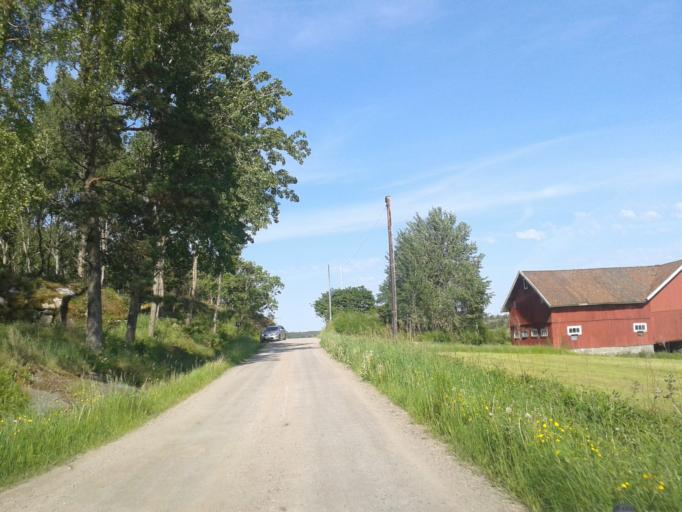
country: SE
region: Vaestra Goetaland
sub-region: Stromstads Kommun
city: Stroemstad
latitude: 58.8620
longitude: 11.2252
